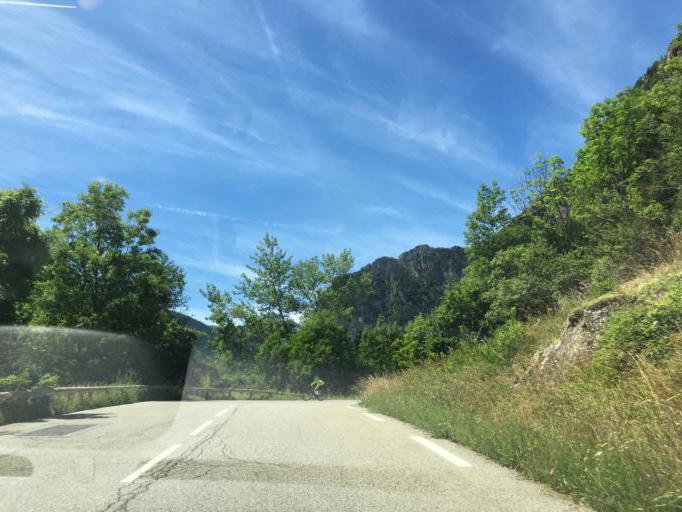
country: IT
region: Piedmont
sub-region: Provincia di Cuneo
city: Sambuco
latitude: 44.2003
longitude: 7.0727
